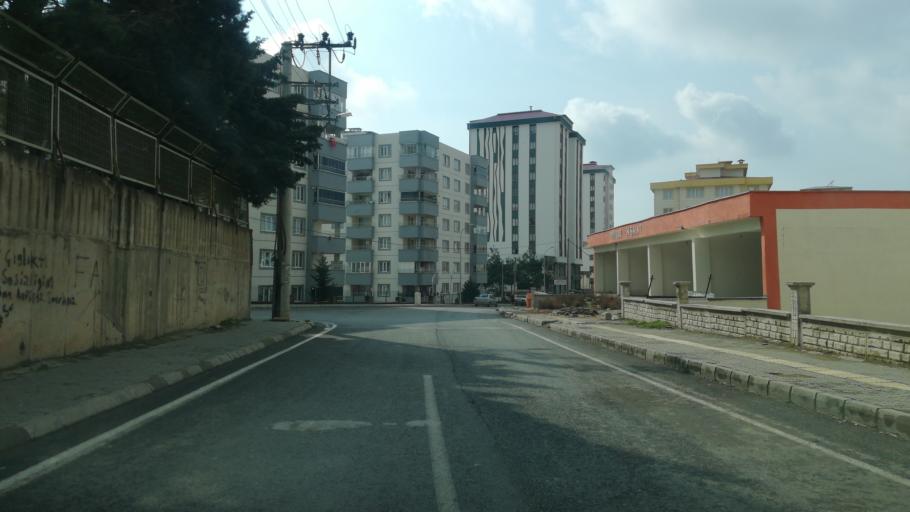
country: TR
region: Kahramanmaras
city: Kahramanmaras
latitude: 37.5791
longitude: 36.8949
